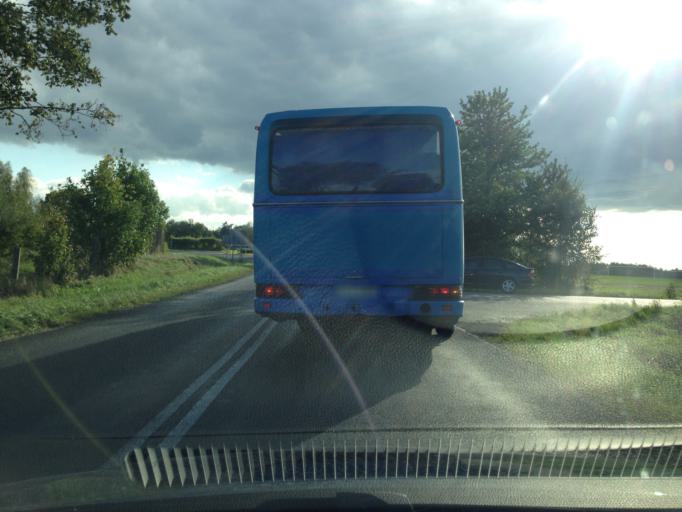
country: PL
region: Kujawsko-Pomorskie
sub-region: Powiat rypinski
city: Rogowo
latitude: 53.0208
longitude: 19.3508
